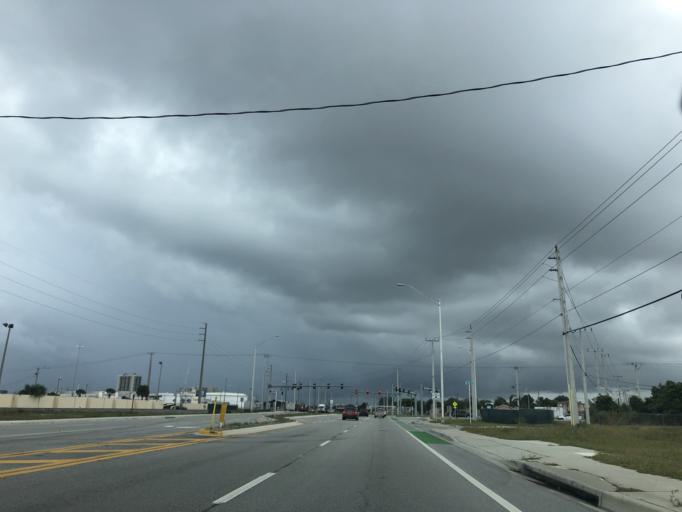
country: US
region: Florida
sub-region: Palm Beach County
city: Riviera Beach
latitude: 26.7706
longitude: -80.0621
